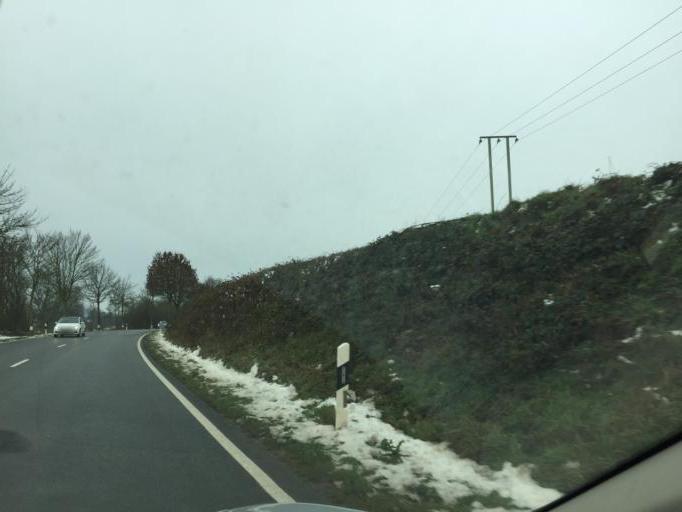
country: LU
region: Diekirch
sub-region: Canton de Diekirch
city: Mertzig
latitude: 49.8423
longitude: 6.0231
